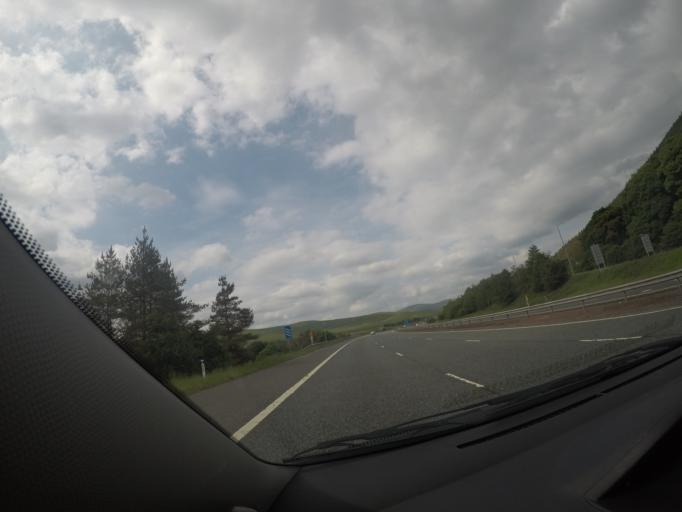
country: GB
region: Scotland
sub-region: South Lanarkshire
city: Biggar
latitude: 55.4432
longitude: -3.6526
